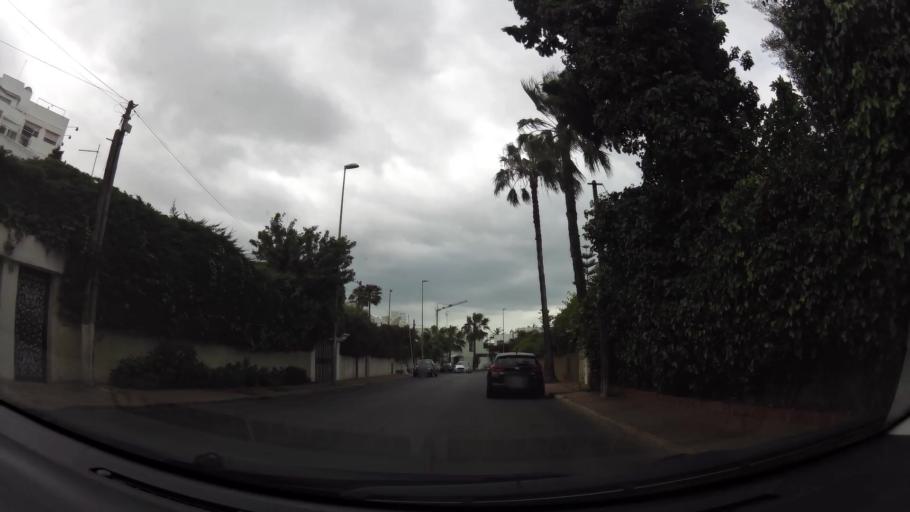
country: MA
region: Grand Casablanca
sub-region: Casablanca
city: Casablanca
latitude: 33.5680
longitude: -7.6570
